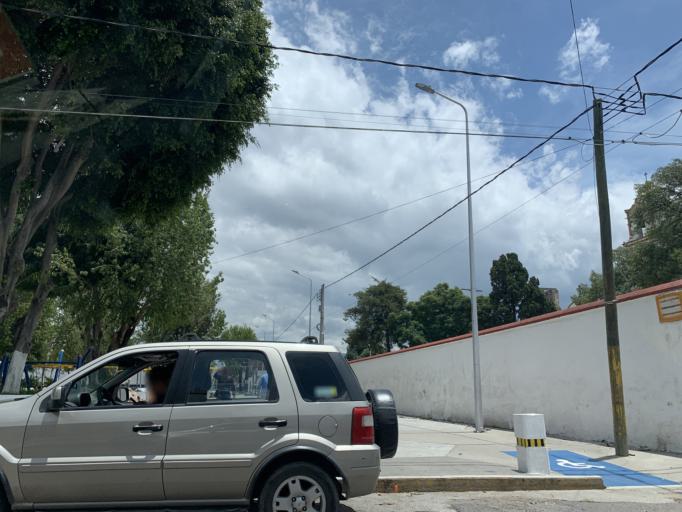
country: MX
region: Puebla
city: Puebla
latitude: 19.0594
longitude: -98.2014
